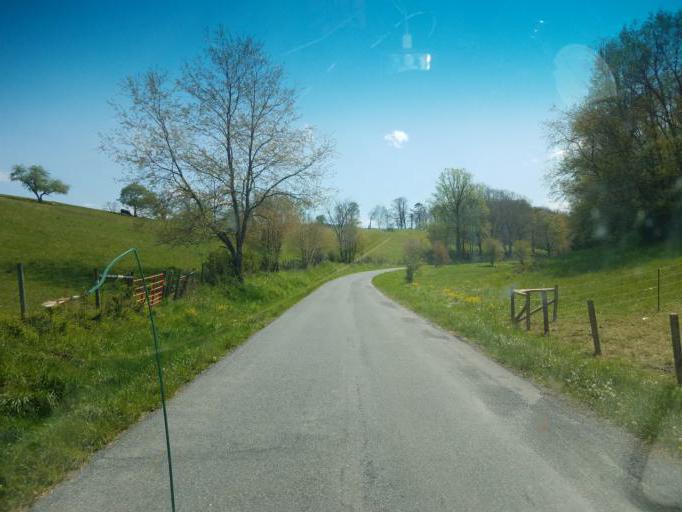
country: US
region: Virginia
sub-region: Smyth County
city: Marion
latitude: 36.7688
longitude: -81.4543
